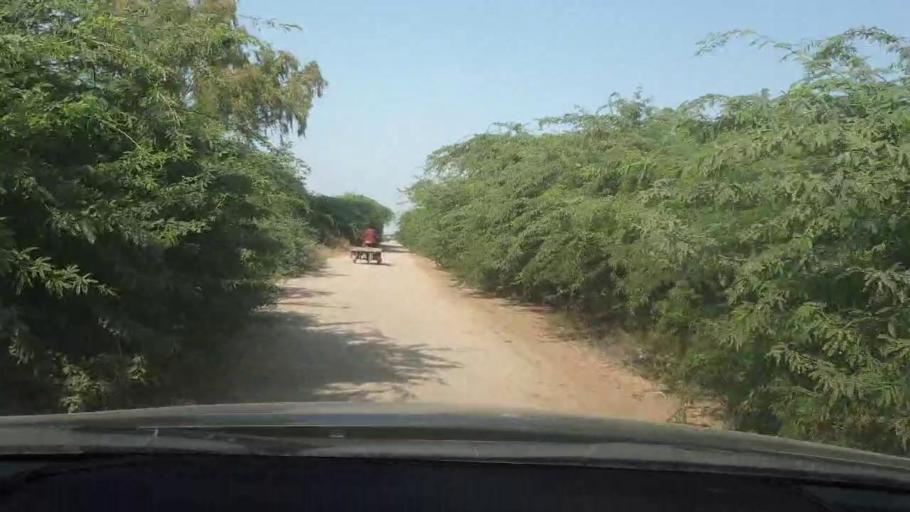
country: PK
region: Sindh
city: Naukot
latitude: 24.7708
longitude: 69.2569
